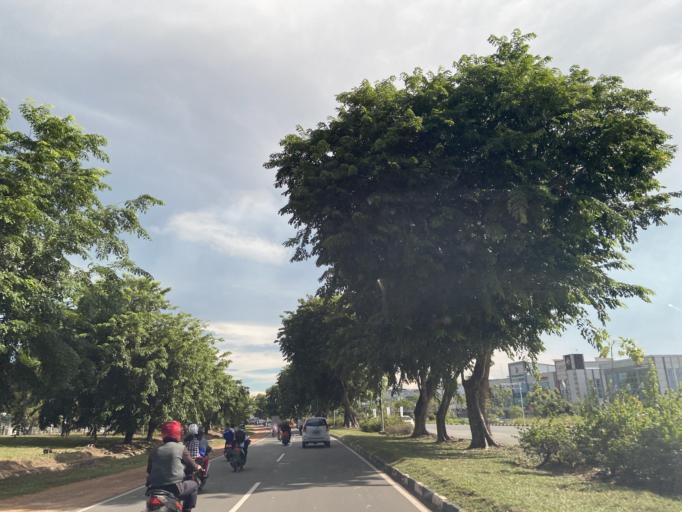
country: SG
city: Singapore
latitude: 1.1135
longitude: 104.0433
